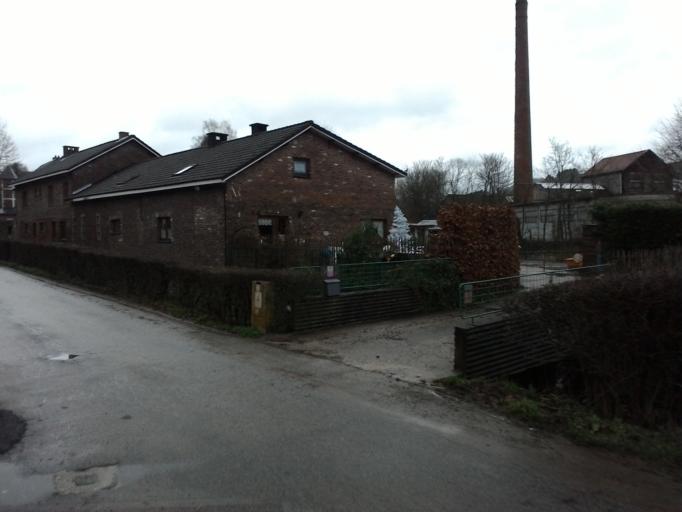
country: BE
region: Wallonia
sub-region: Province de Liege
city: Stavelot
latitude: 50.3927
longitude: 5.9321
